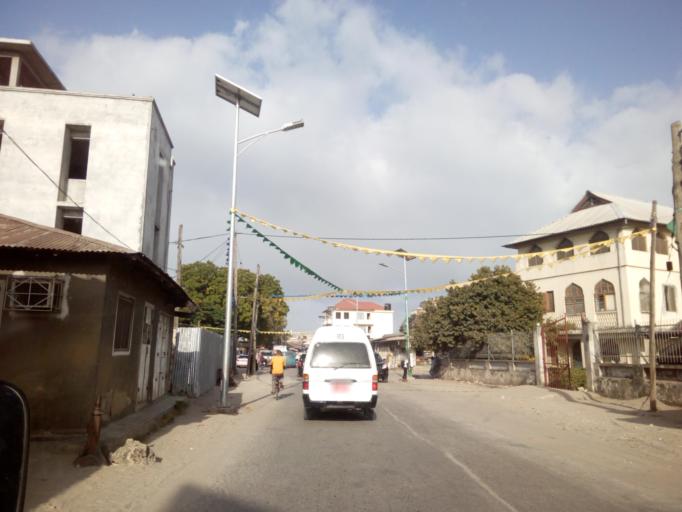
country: TZ
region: Zanzibar Urban/West
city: Zanzibar
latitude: -6.1623
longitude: 39.2054
